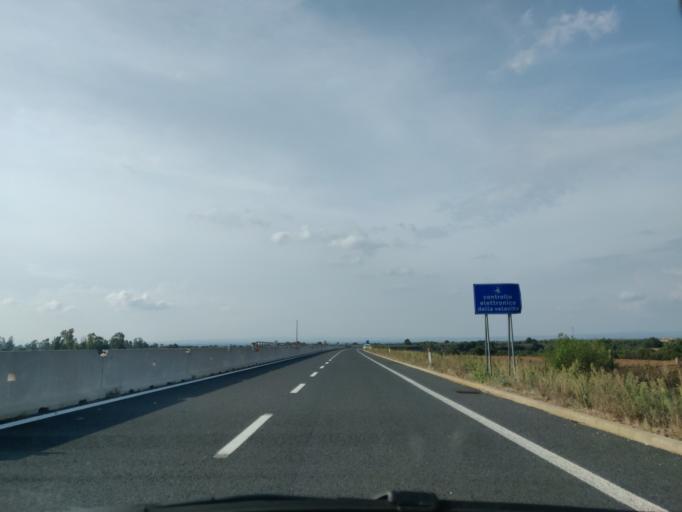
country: IT
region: Latium
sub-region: Provincia di Viterbo
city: Blera
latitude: 42.3261
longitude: 11.9875
